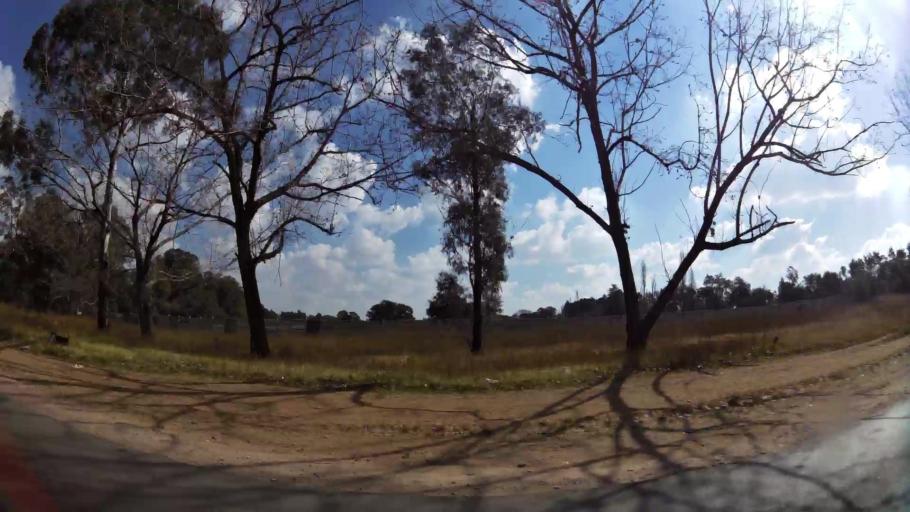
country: ZA
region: Gauteng
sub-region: City of Johannesburg Metropolitan Municipality
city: Roodepoort
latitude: -26.1775
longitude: 27.8713
